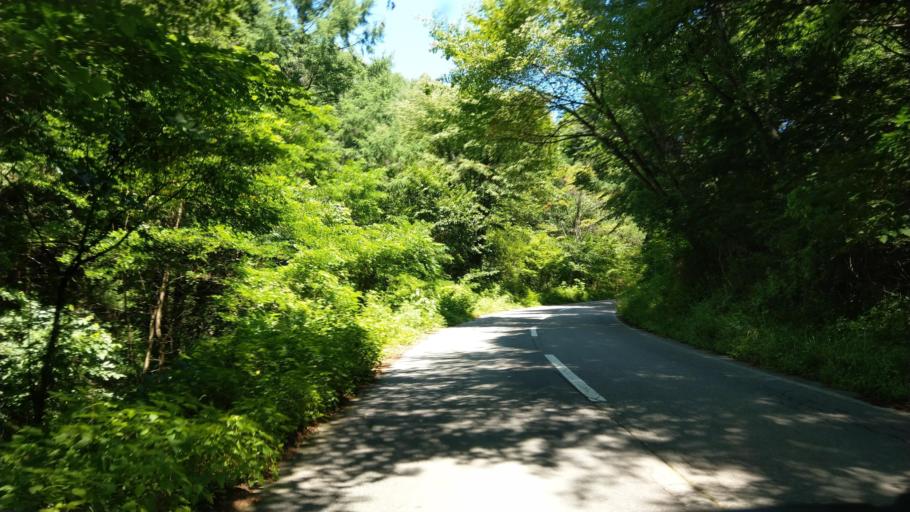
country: JP
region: Nagano
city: Komoro
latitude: 36.3650
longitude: 138.4574
